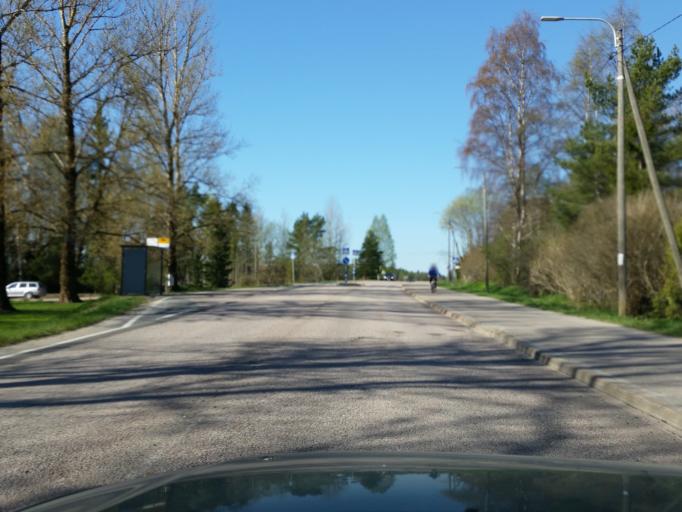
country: FI
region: Uusimaa
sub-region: Helsinki
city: Kirkkonummi
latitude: 60.1350
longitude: 24.5031
